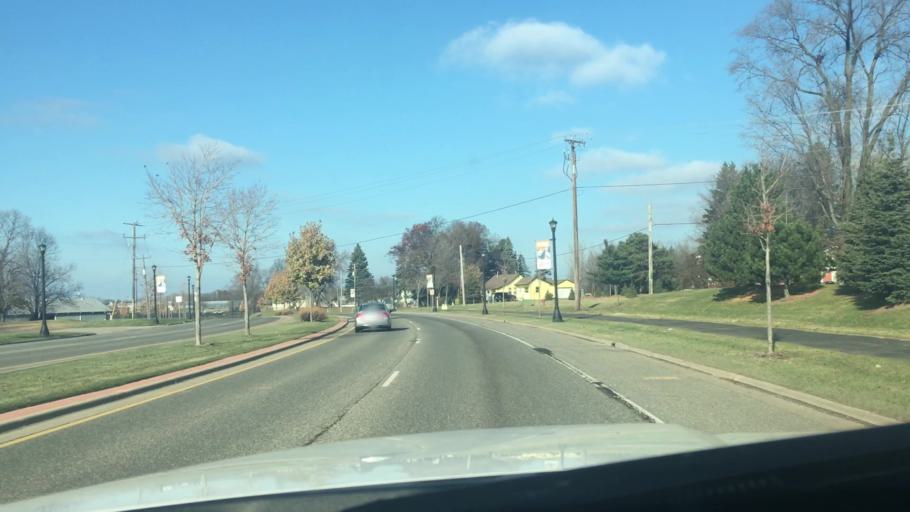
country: US
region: Minnesota
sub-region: Washington County
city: Hugo
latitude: 45.1595
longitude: -92.9988
